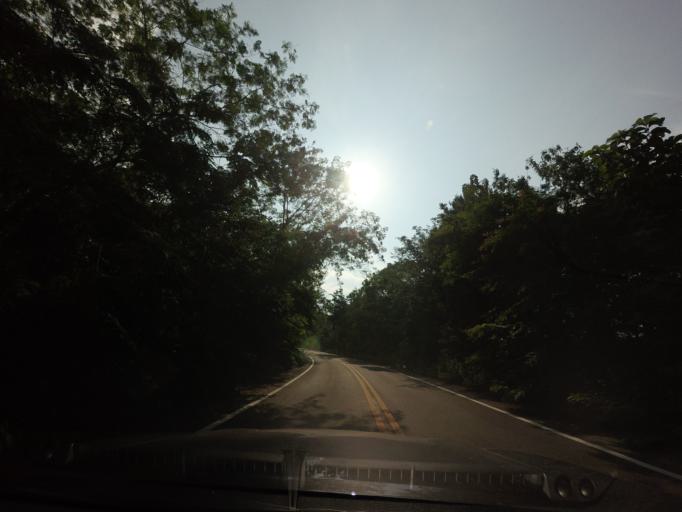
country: TH
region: Nan
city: Na Noi
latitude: 18.3636
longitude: 100.8702
